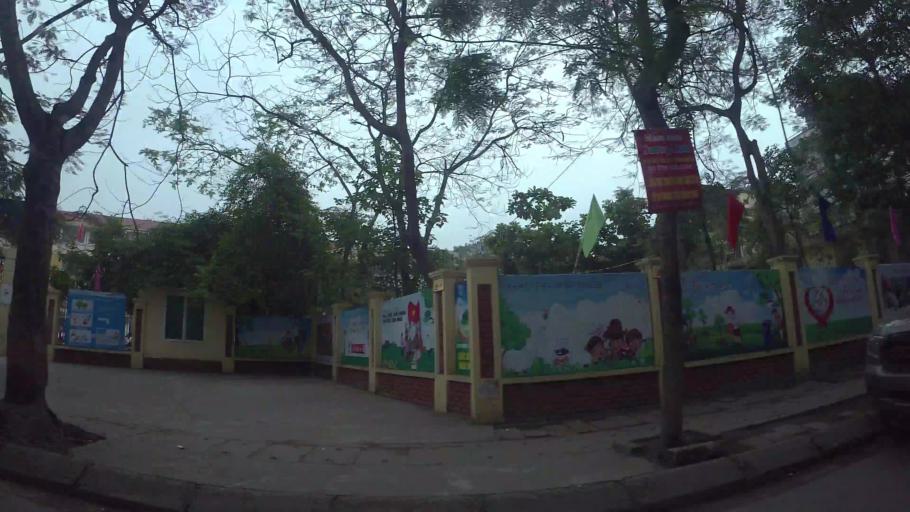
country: VN
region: Ha Noi
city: Hai BaTrung
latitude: 20.9860
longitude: 105.8593
